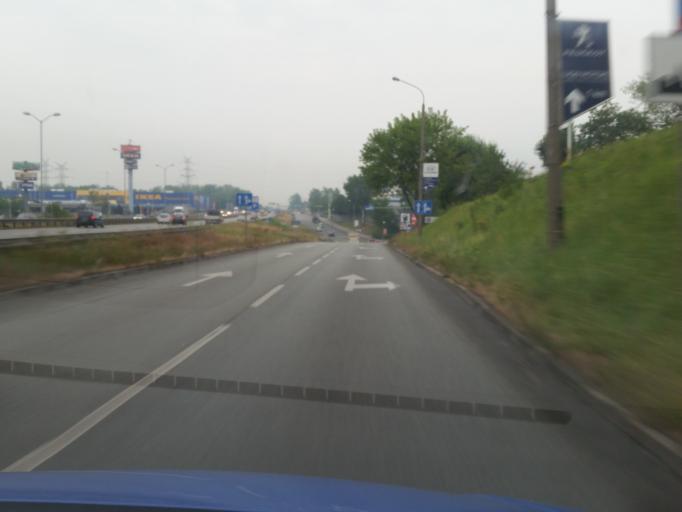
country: PL
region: Silesian Voivodeship
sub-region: Katowice
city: Katowice
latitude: 50.2672
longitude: 19.0551
